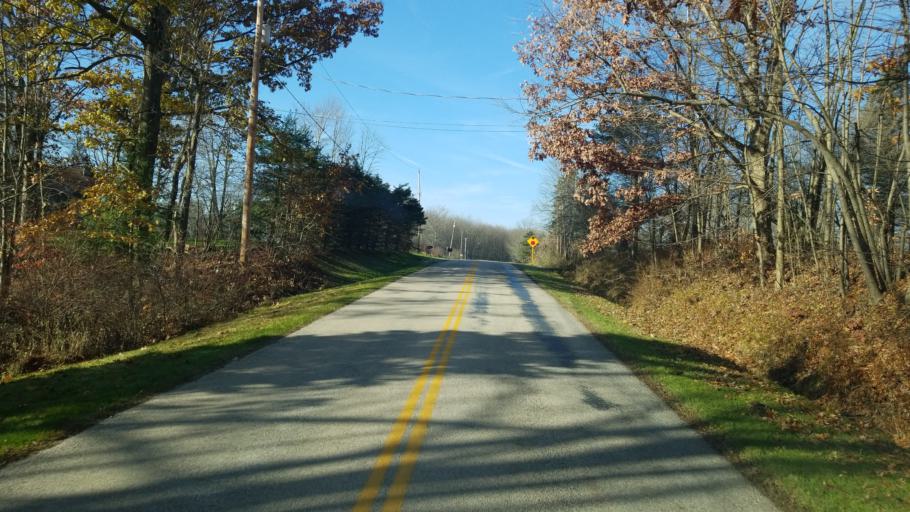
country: US
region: Ohio
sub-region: Ashtabula County
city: Edgewood
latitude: 41.8230
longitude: -80.7142
